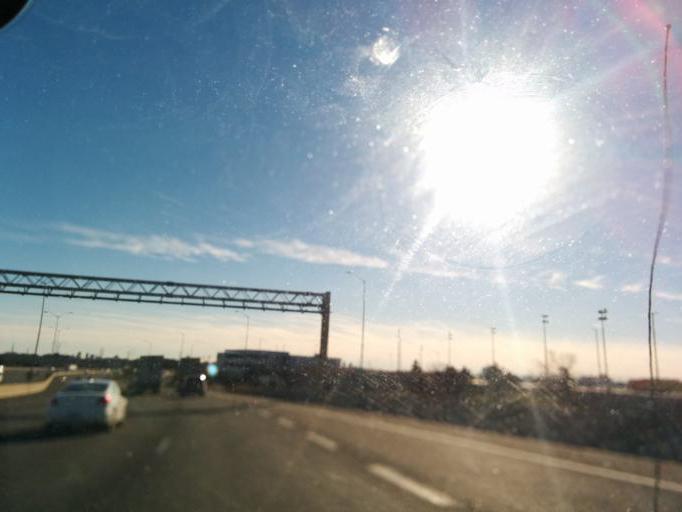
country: CA
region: Ontario
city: Etobicoke
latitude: 43.6846
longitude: -79.5998
